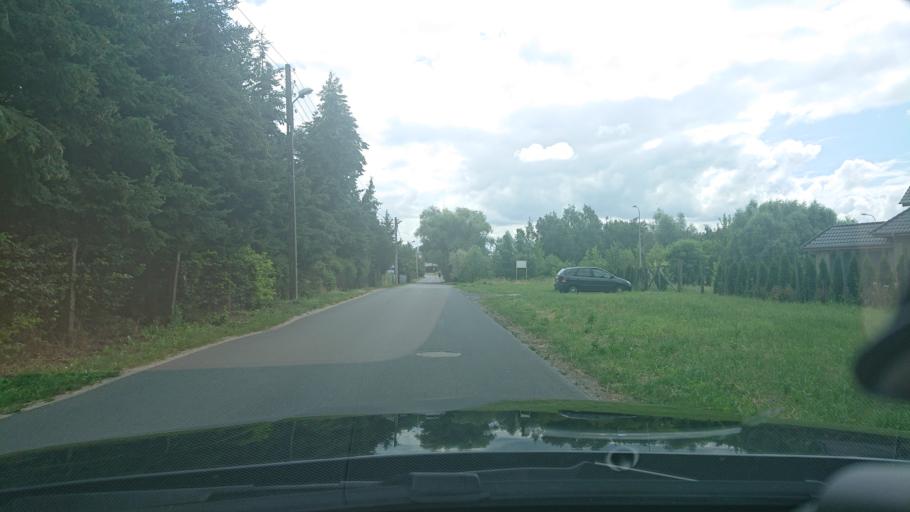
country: PL
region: Greater Poland Voivodeship
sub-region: Powiat gnieznienski
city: Gniezno
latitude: 52.5178
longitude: 17.6197
